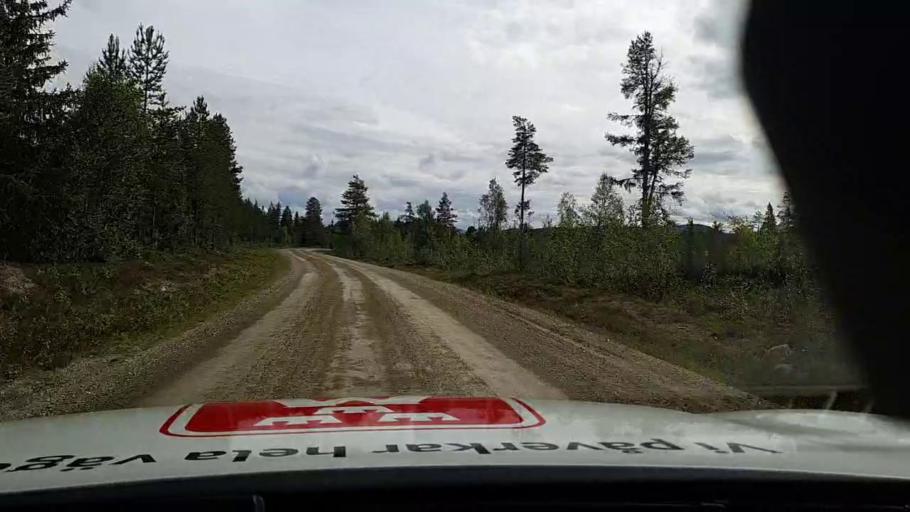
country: SE
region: Jaemtland
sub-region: Are Kommun
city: Jarpen
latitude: 62.5263
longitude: 13.4877
